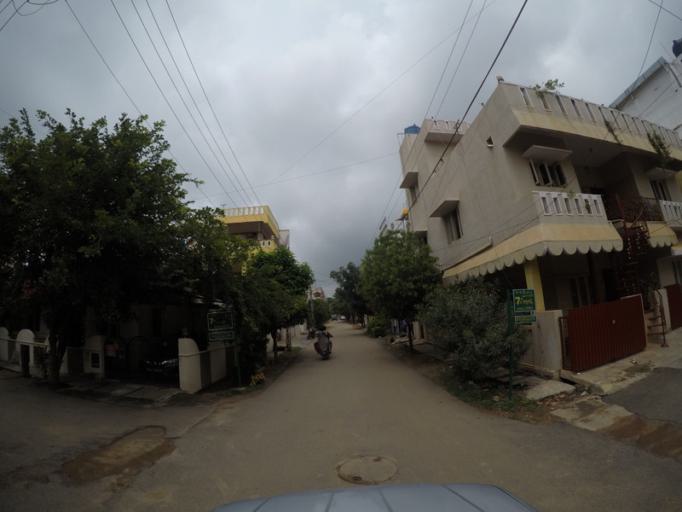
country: IN
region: Karnataka
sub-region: Bangalore Urban
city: Yelahanka
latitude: 13.0686
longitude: 77.5566
